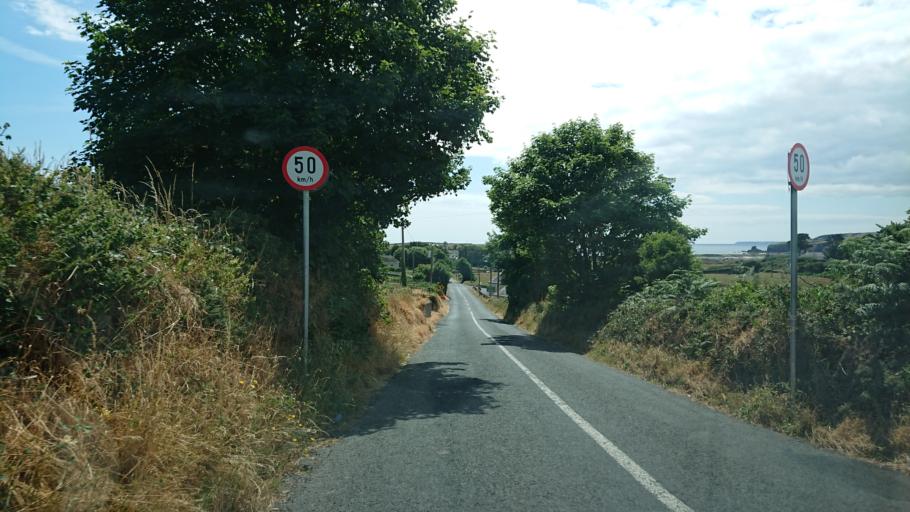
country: IE
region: Munster
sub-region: Waterford
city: Portlaw
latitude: 52.1452
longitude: -7.3560
